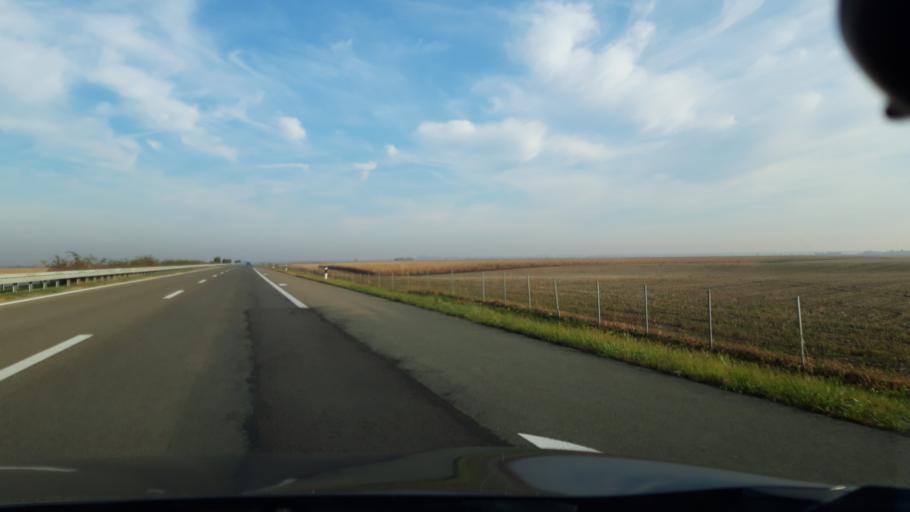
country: RS
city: Zmajevo
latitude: 45.4771
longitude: 19.7293
